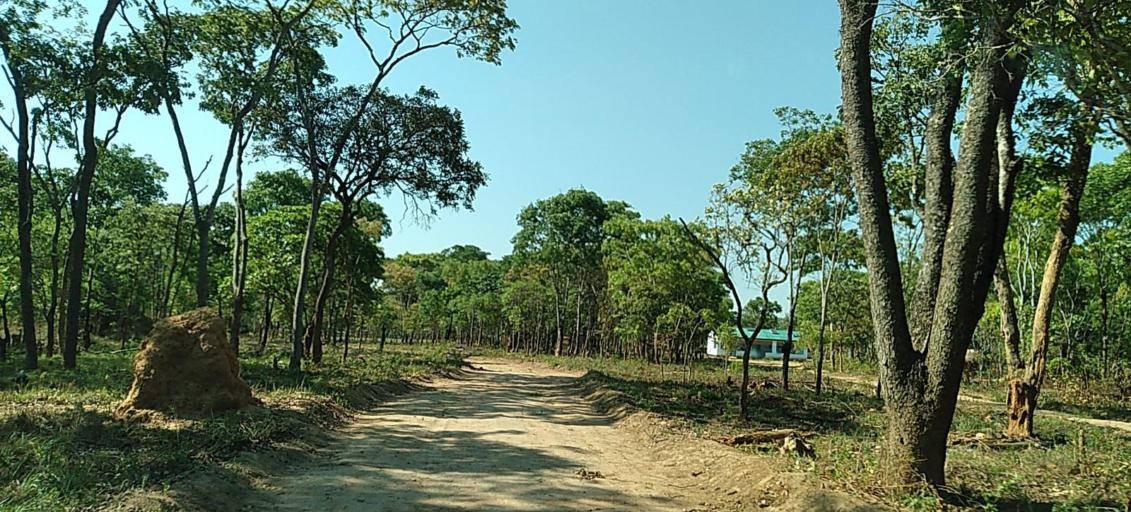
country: ZM
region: Central
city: Mkushi
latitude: -13.4727
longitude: 28.9801
